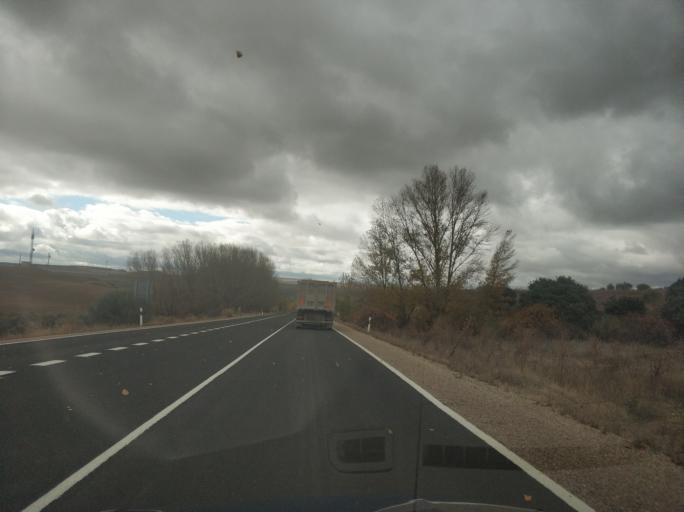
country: ES
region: Castille and Leon
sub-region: Provincia de Zamora
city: Castrillo de la Guarena
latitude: 41.2356
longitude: -5.3043
